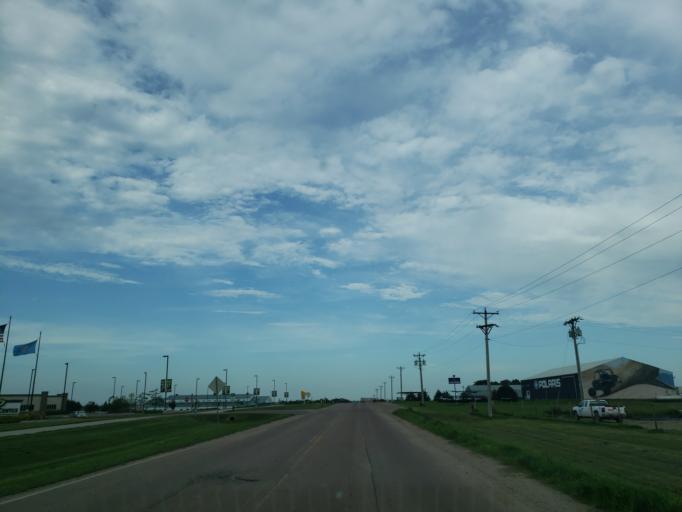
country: US
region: South Dakota
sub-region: Davison County
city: Mitchell
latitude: 43.6877
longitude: -98.0043
